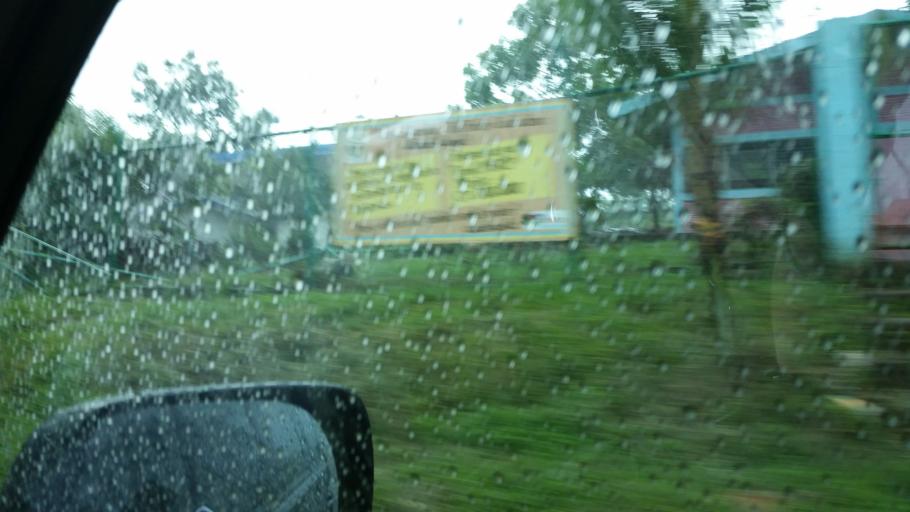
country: NI
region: Atlantico Norte (RAAN)
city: Waslala
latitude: 13.1566
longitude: -85.4381
